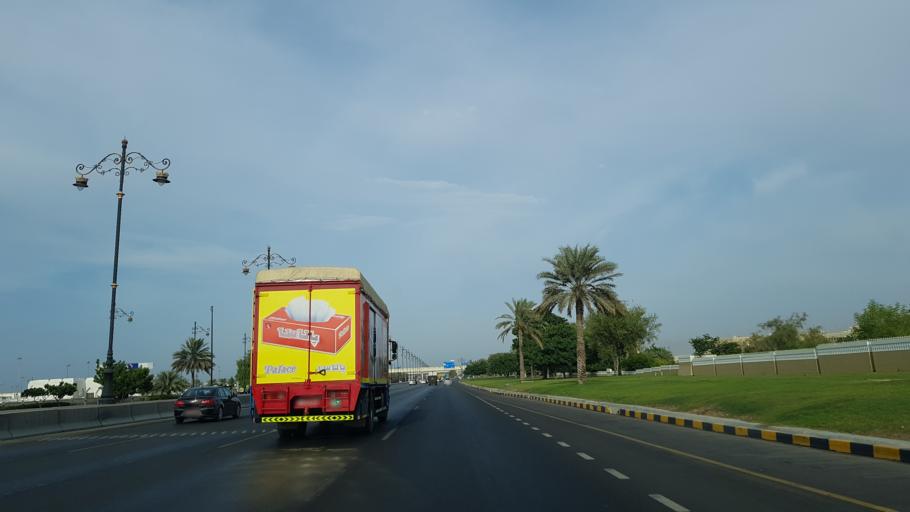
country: OM
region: Muhafazat Masqat
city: Bawshar
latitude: 23.5853
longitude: 58.2866
